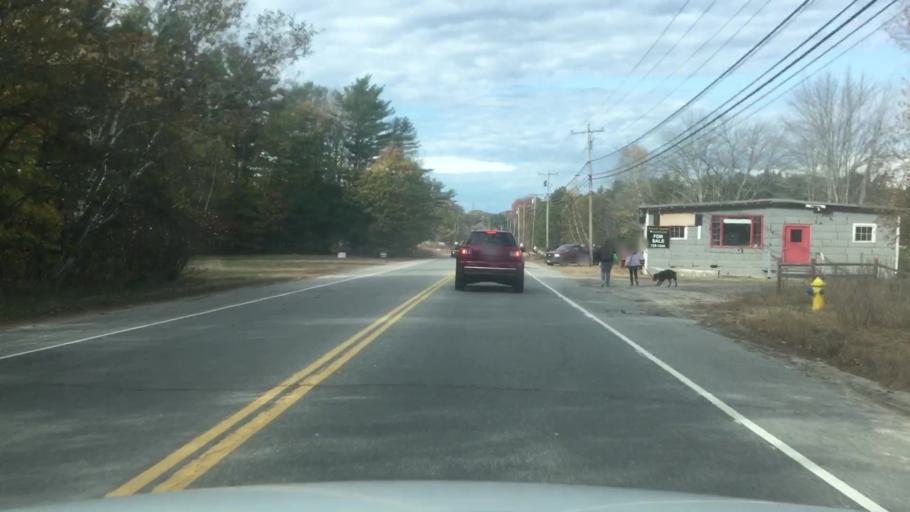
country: US
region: Maine
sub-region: Sagadahoc County
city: Bath
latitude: 43.9130
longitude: -69.8826
